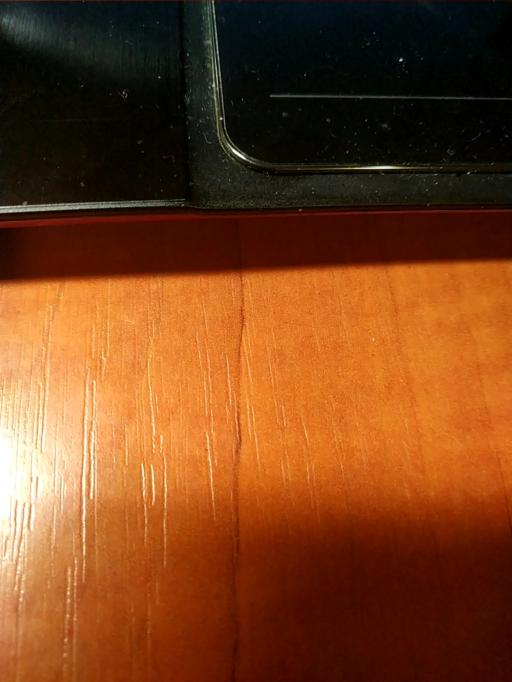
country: RU
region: Tverskaya
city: Likhoslavl'
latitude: 57.1744
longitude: 35.5088
